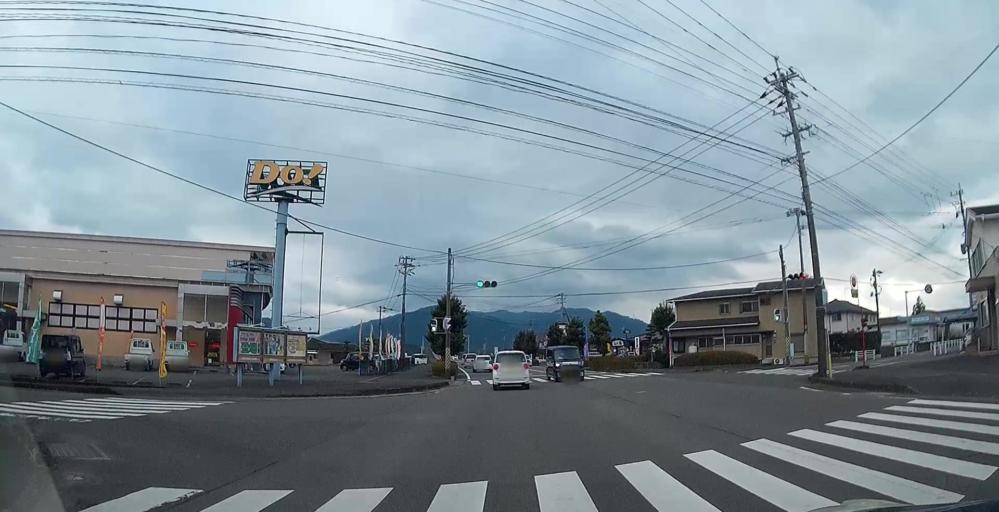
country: JP
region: Kagoshima
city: Izumi
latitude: 32.0811
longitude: 130.3445
